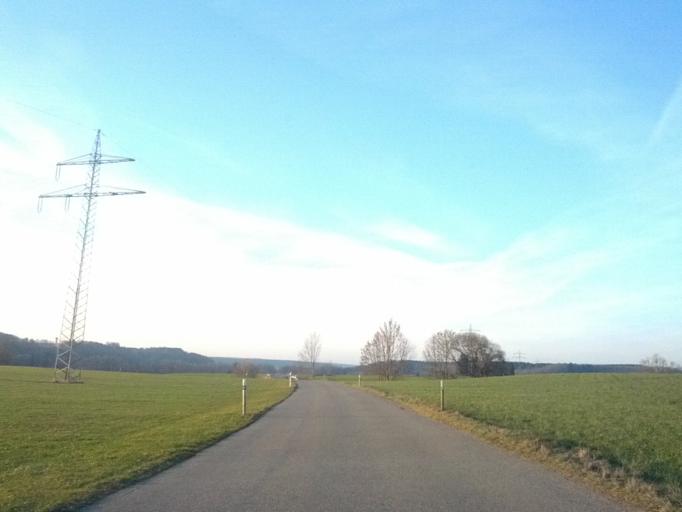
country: DE
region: Bavaria
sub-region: Swabia
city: Kronburg
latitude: 47.8811
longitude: 10.1694
